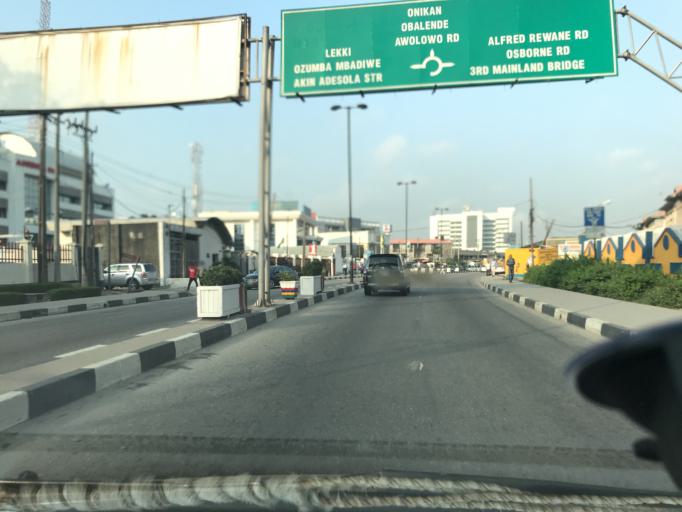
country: NG
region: Lagos
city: Ikoyi
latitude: 6.4439
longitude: 3.4307
